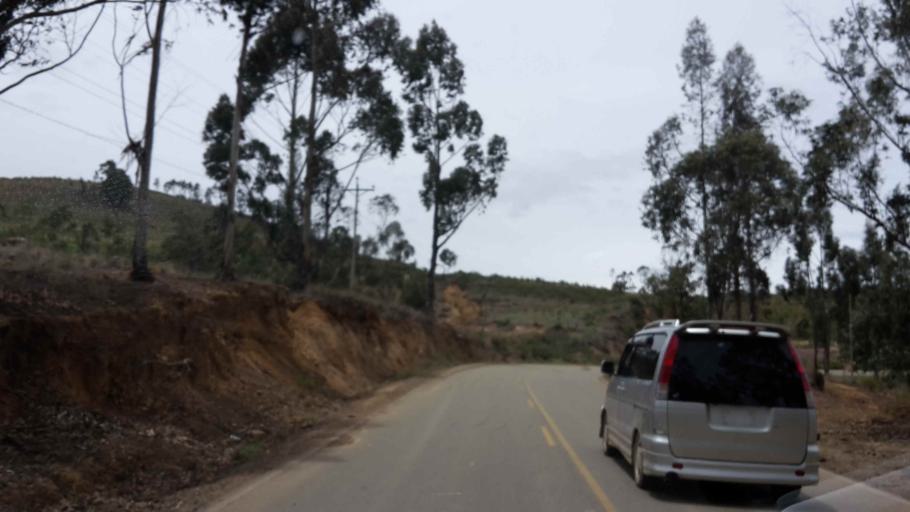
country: BO
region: Cochabamba
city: Totora
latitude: -17.7137
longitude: -65.2086
